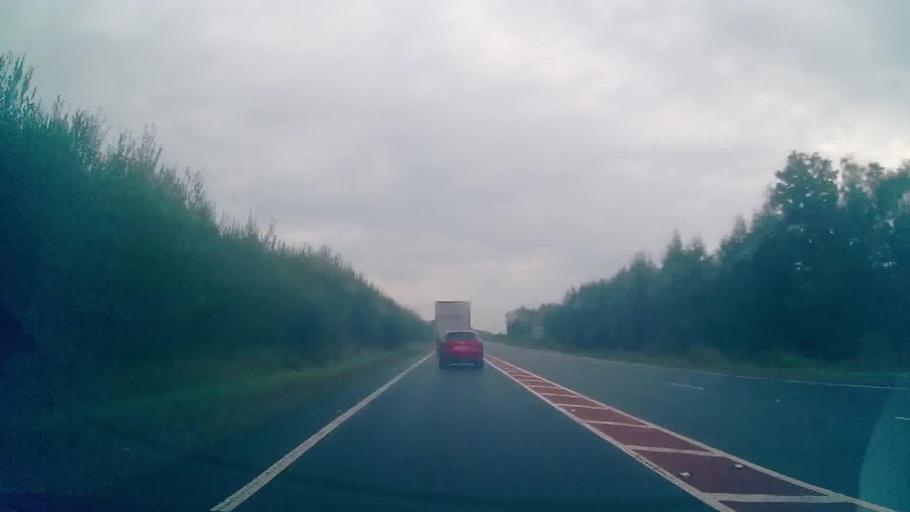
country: GB
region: Scotland
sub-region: Dumfries and Galloway
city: Lockerbie
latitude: 55.0309
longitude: -3.3976
